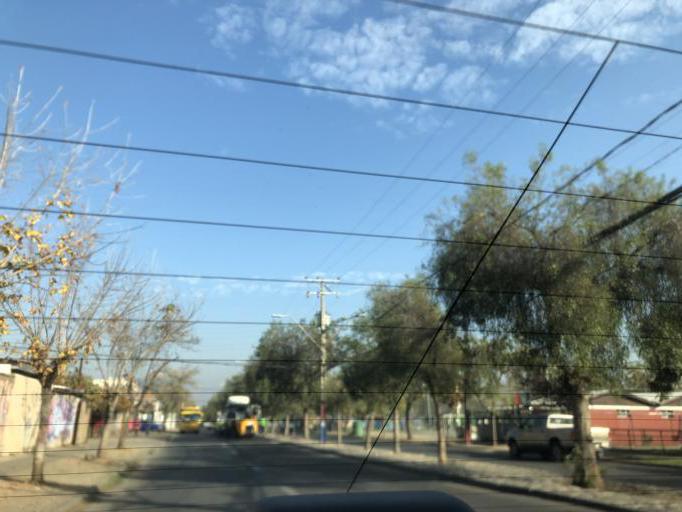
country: CL
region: Santiago Metropolitan
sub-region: Provincia de Cordillera
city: Puente Alto
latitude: -33.5939
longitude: -70.5745
